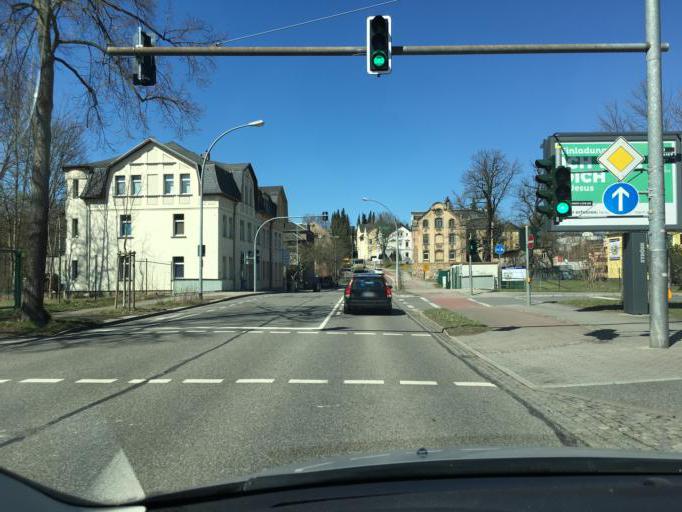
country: DE
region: Saxony
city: Neukirchen
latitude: 50.8167
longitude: 12.8409
